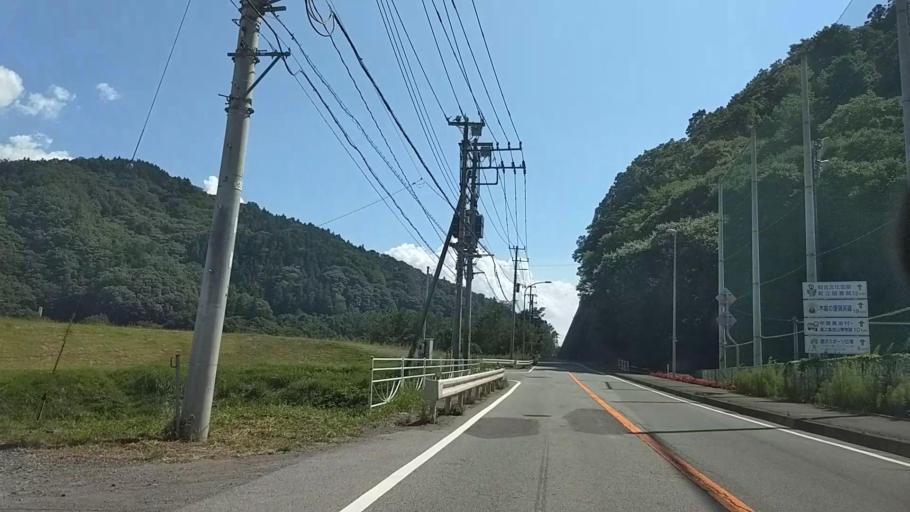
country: JP
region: Yamanashi
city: Ryuo
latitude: 35.4720
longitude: 138.4437
